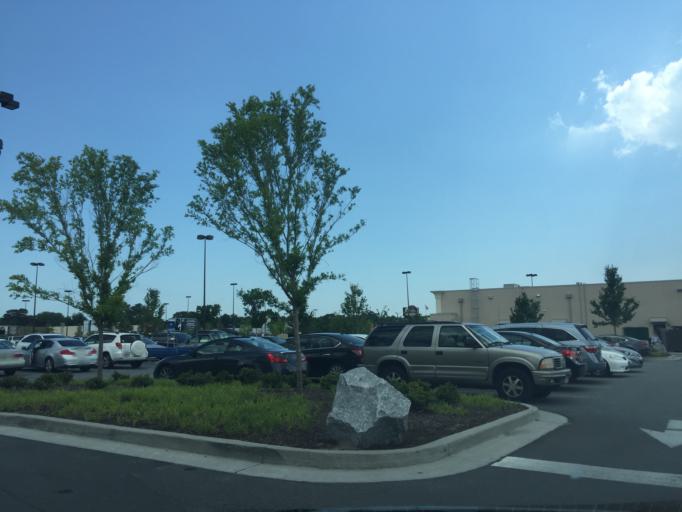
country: US
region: Georgia
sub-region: Chatham County
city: Isle of Hope
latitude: 32.0060
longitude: -81.1139
